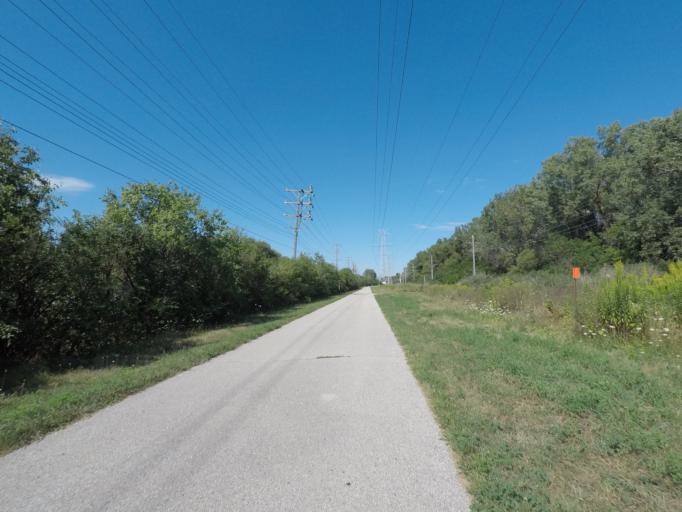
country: US
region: Wisconsin
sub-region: Waukesha County
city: New Berlin
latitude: 43.0101
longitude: -88.1151
